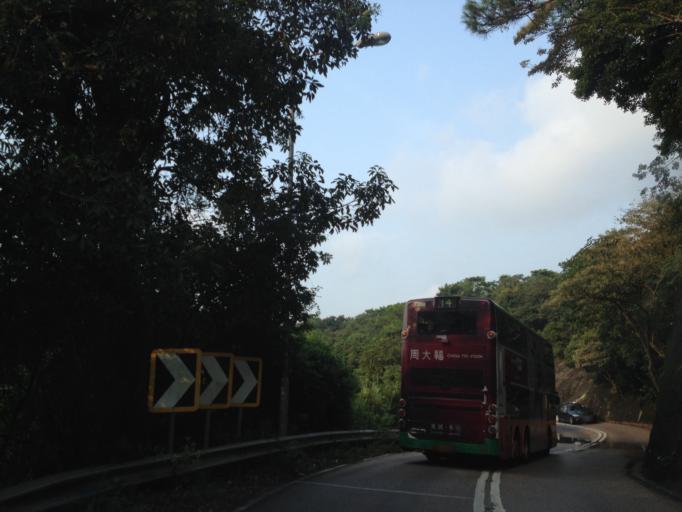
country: HK
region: Wanchai
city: Wan Chai
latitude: 22.2410
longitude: 114.2215
